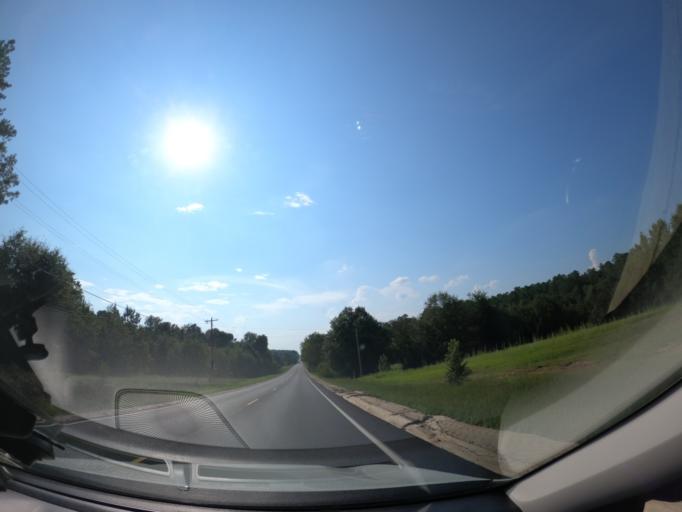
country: US
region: South Carolina
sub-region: Aiken County
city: New Ellenton
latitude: 33.3960
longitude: -81.7449
